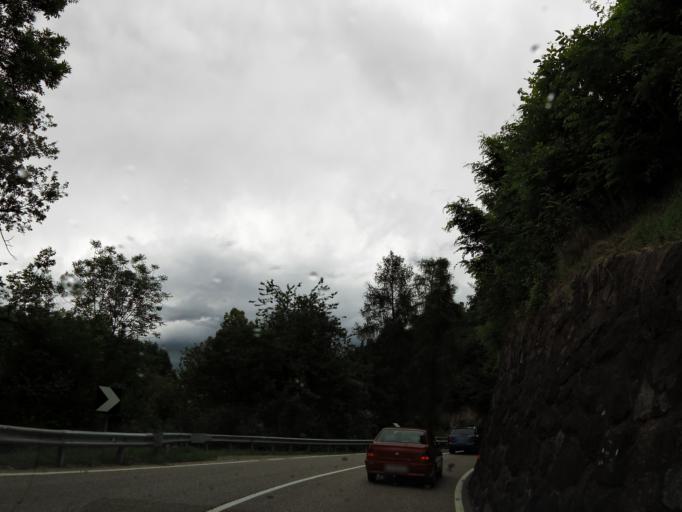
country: IT
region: Trentino-Alto Adige
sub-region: Bolzano
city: Fie Allo Sciliar
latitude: 46.5121
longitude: 11.5071
